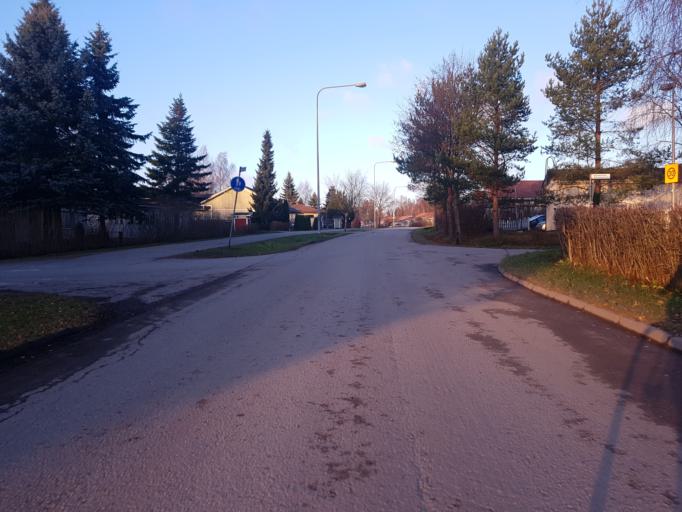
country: FI
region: Uusimaa
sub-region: Helsinki
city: Helsinki
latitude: 60.2747
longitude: 24.9125
